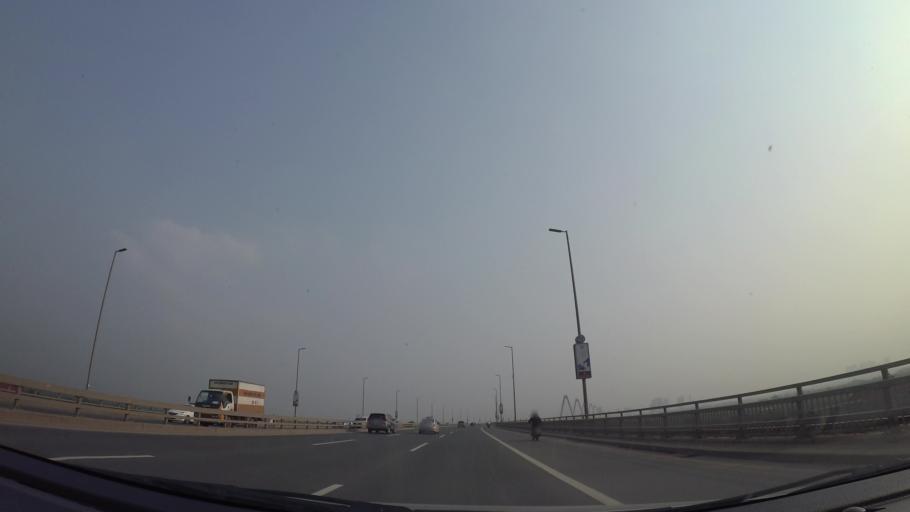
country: VN
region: Ha Noi
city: Dong Anh
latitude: 21.1104
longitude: 105.8270
